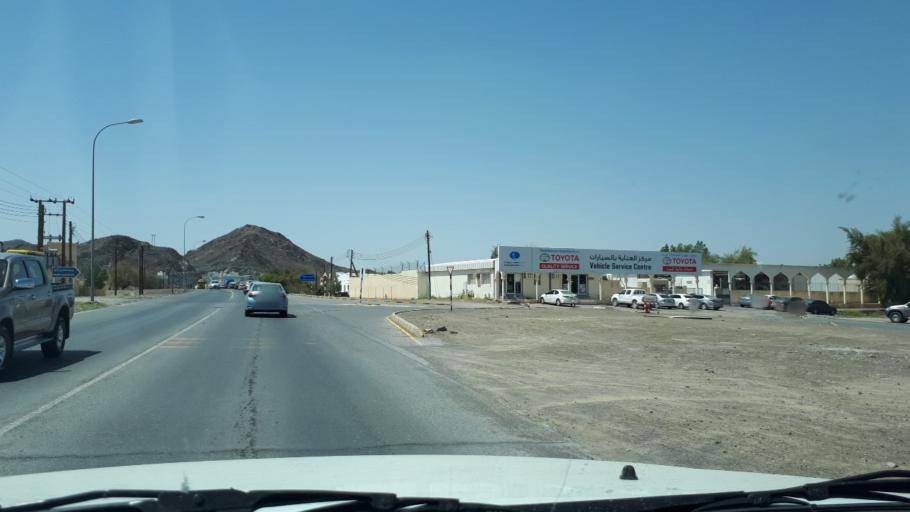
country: OM
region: Muhafazat ad Dakhiliyah
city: Bahla'
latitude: 22.9848
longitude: 57.3090
